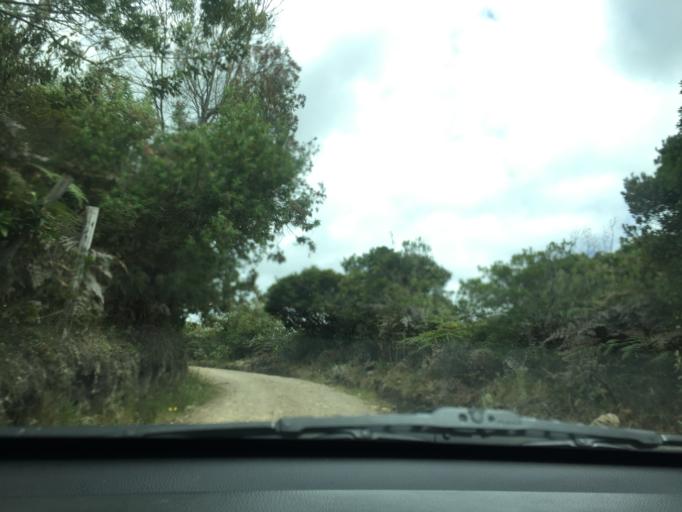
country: CO
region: Cundinamarca
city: Tocancipa
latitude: 4.9594
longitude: -73.8898
